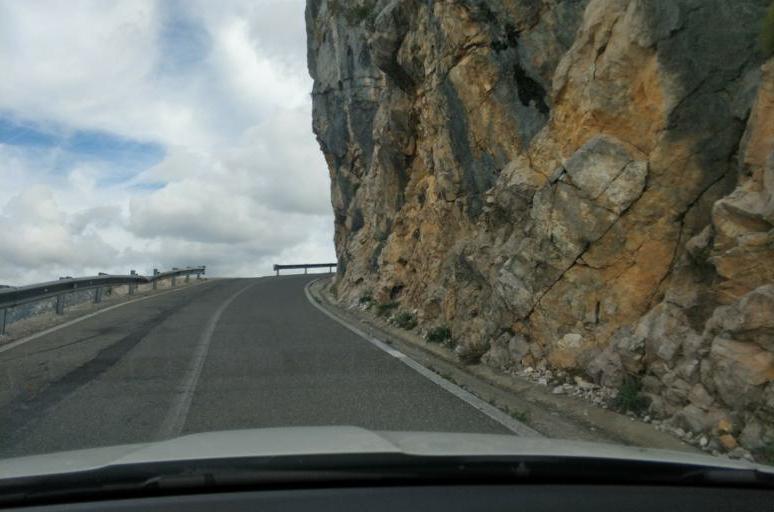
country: AL
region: Durres
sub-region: Rrethi i Krujes
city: Kruje
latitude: 41.5275
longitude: 19.7940
